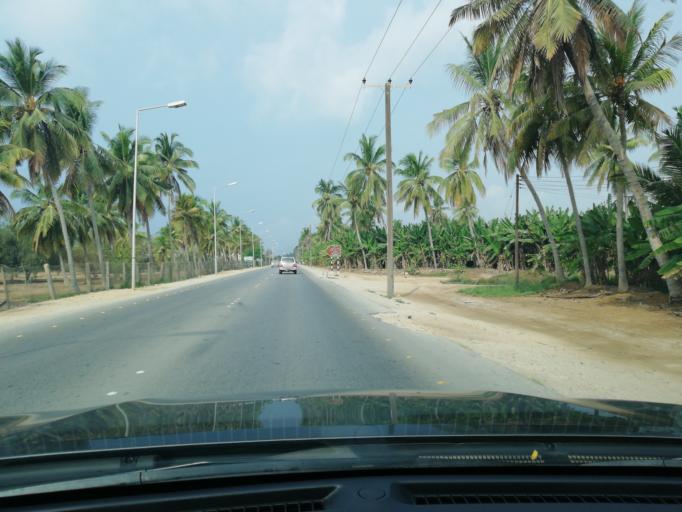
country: OM
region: Zufar
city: Salalah
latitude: 17.0109
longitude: 54.1390
